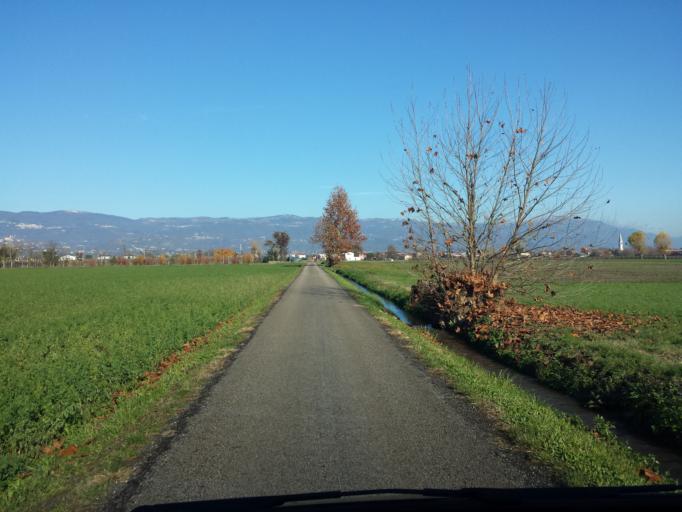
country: IT
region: Veneto
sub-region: Provincia di Vicenza
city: Sandrigo
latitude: 45.6805
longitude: 11.5969
